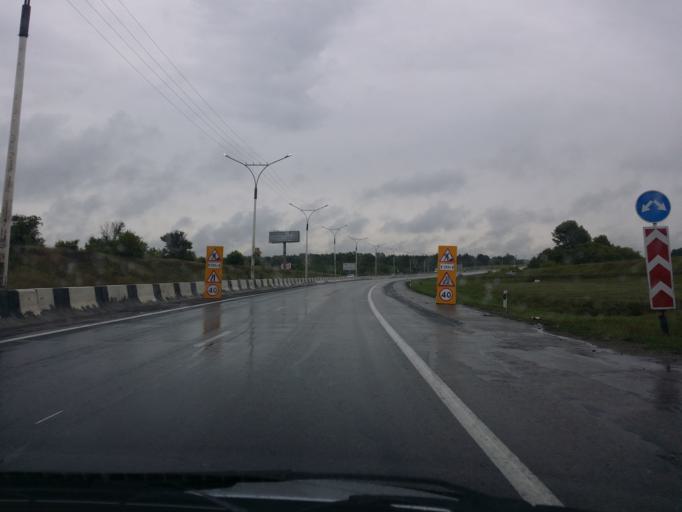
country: RU
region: Altai Krai
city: Novoaltaysk
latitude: 53.3711
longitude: 83.9561
